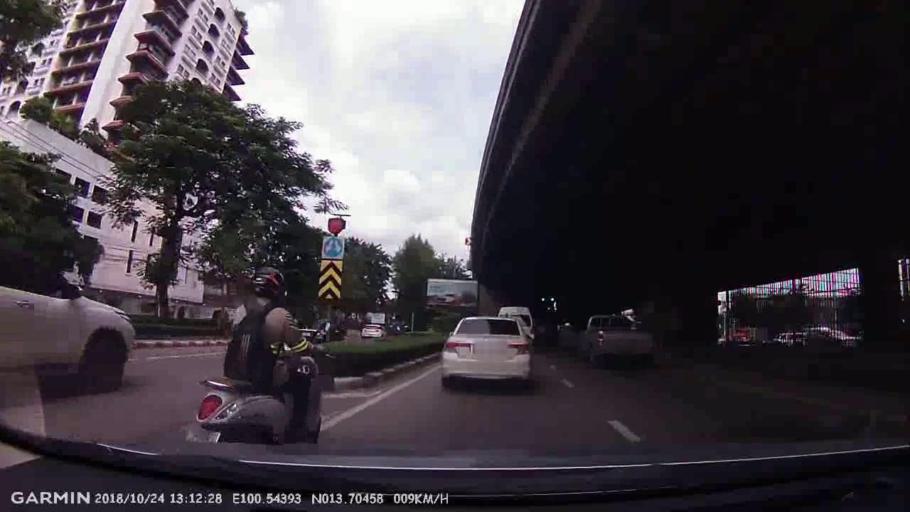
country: TH
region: Bangkok
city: Yan Nawa
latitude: 13.7046
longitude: 100.5439
